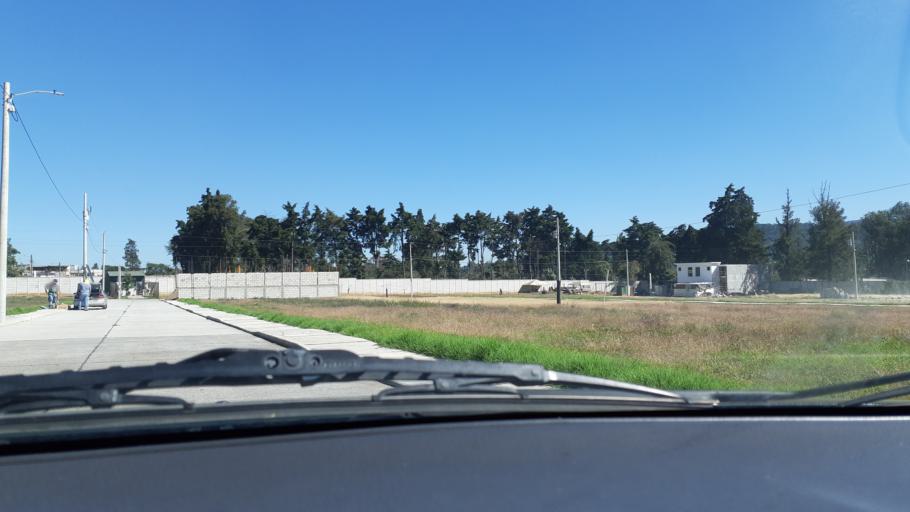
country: GT
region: Chimaltenango
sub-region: Municipio de Chimaltenango
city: Chimaltenango
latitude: 14.6572
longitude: -90.8053
